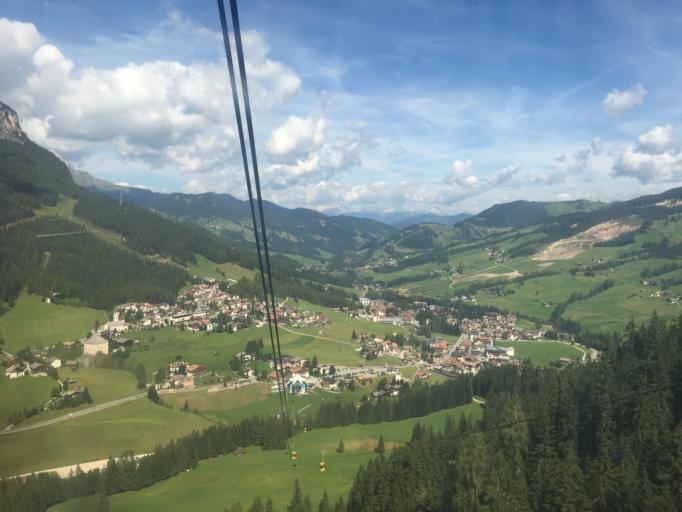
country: IT
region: Trentino-Alto Adige
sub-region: Bolzano
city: Badia
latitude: 46.5740
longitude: 11.9033
